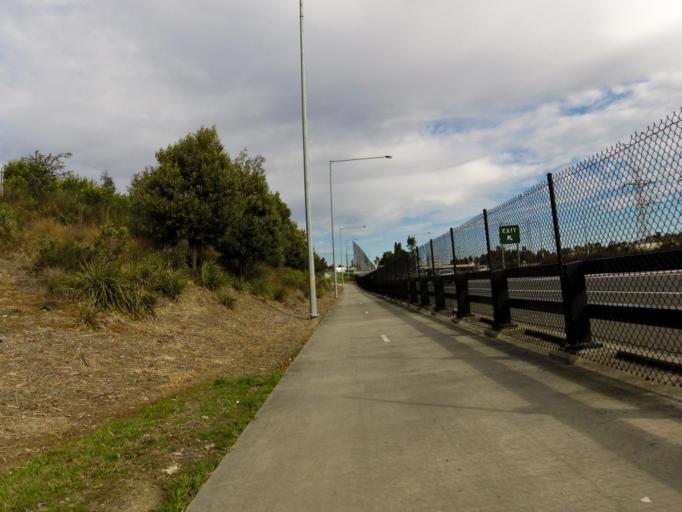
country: AU
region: Victoria
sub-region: Knox
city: Wantirna
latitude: -37.8292
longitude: 145.2179
